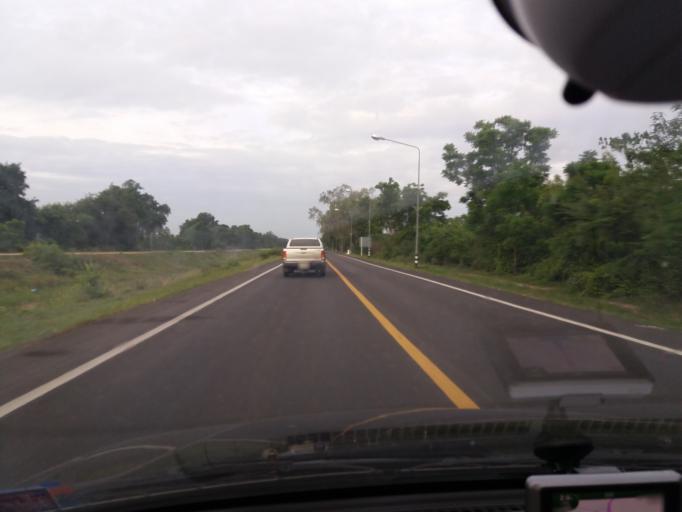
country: TH
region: Suphan Buri
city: Don Chedi
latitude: 14.5293
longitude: 99.9307
